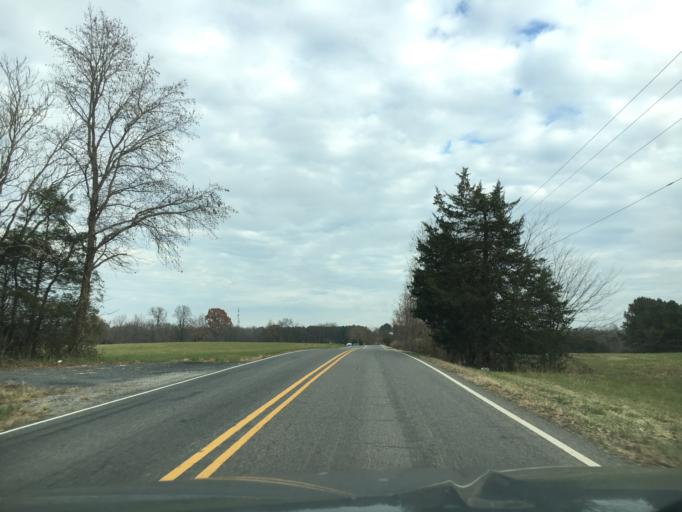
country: US
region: Virginia
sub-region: Cumberland County
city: Cumberland
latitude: 37.4585
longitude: -78.2912
